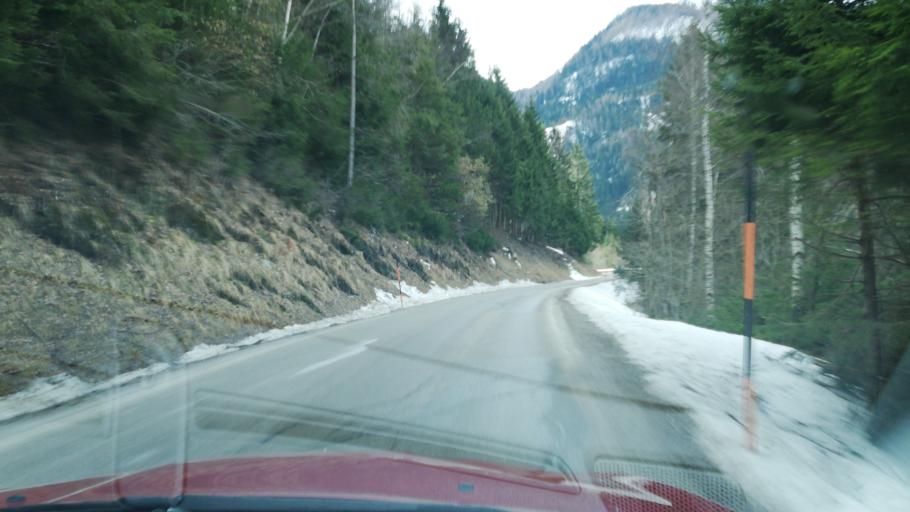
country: AT
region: Styria
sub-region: Politischer Bezirk Liezen
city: Donnersbach
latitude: 47.4413
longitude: 14.1407
